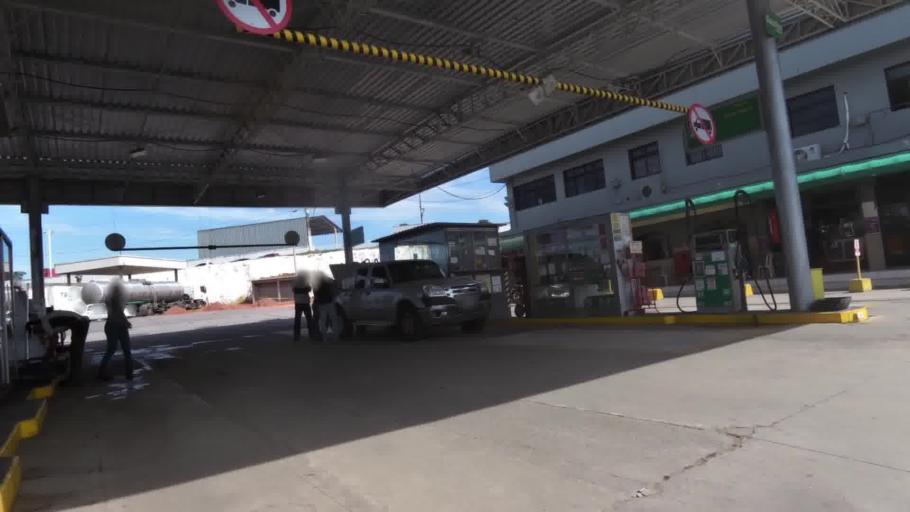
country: BR
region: Espirito Santo
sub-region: Vitoria
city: Vitoria
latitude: -20.2509
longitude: -40.3733
